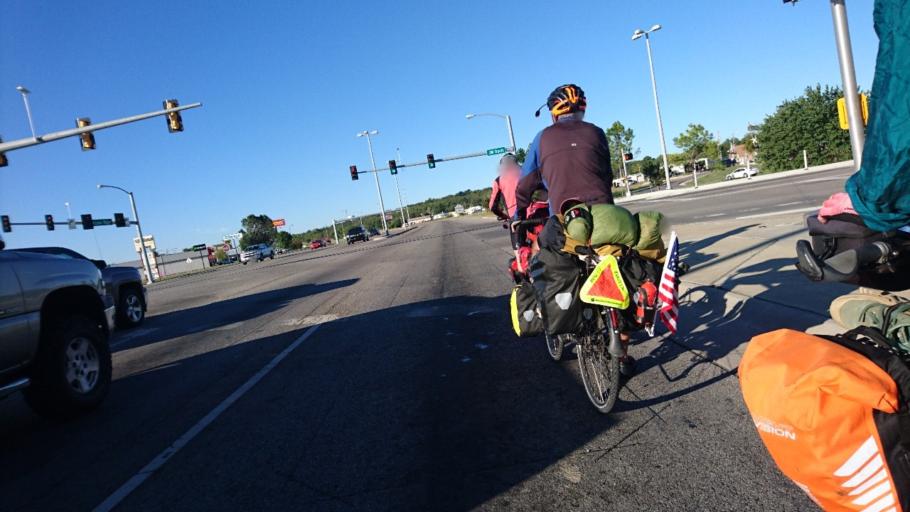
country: US
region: Oklahoma
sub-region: Rogers County
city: Claremore
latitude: 36.3074
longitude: -95.6200
